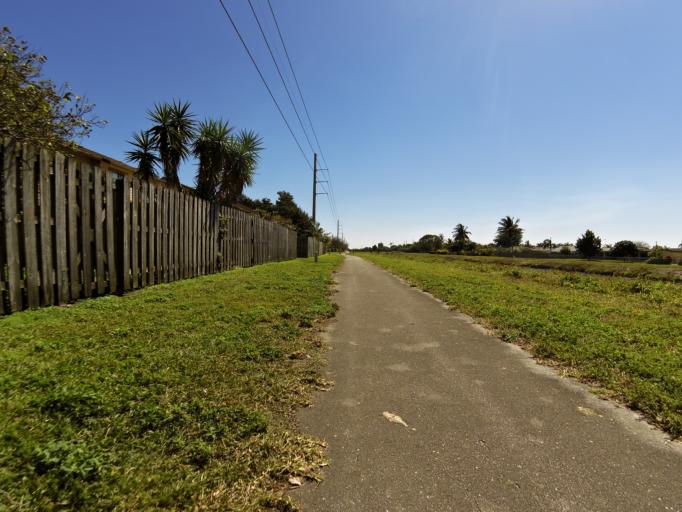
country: US
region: Florida
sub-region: Broward County
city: Tamarac
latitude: 26.1720
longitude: -80.2978
